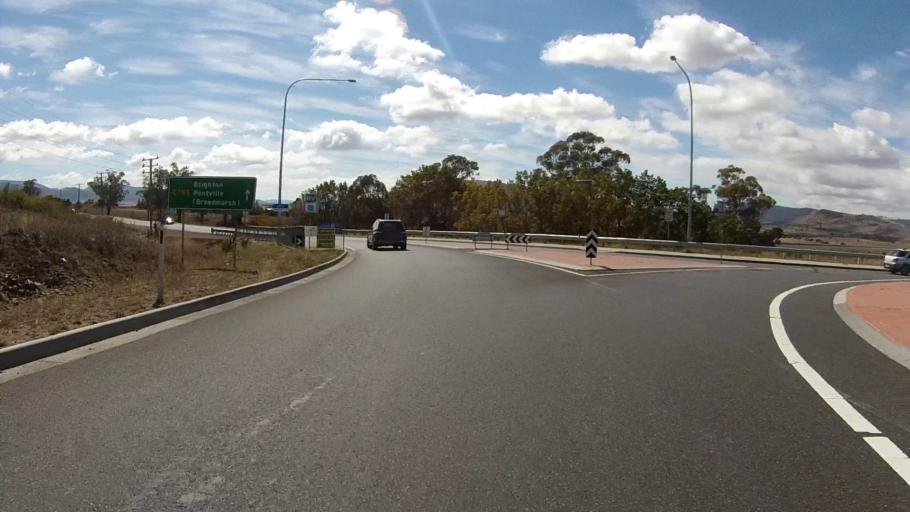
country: AU
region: Tasmania
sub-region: Brighton
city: Bridgewater
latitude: -42.7125
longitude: 147.2435
